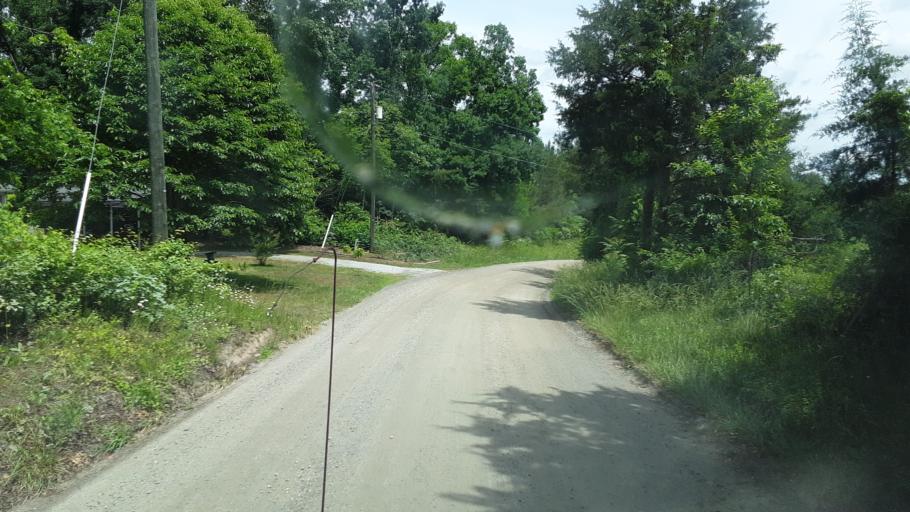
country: US
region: Virginia
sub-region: Pittsylvania County
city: Chatham
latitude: 36.8407
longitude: -79.4324
